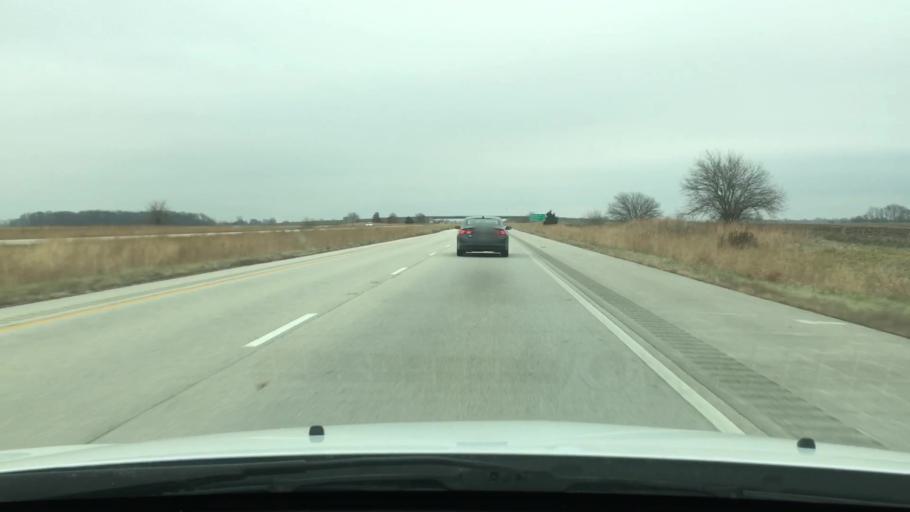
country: US
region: Illinois
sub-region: Sangamon County
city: New Berlin
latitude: 39.7402
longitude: -89.9098
